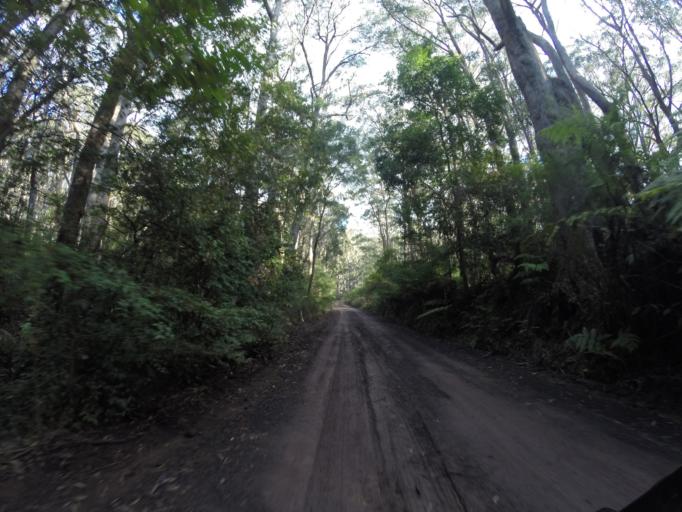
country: AU
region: New South Wales
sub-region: Wollongong
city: Cordeaux Heights
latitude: -34.4154
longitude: 150.7840
